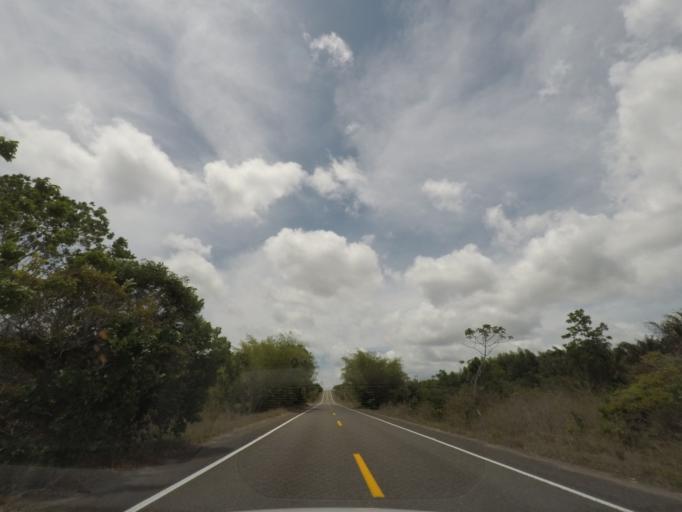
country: BR
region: Sergipe
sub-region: Indiaroba
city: Indiaroba
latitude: -11.6612
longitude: -37.5536
